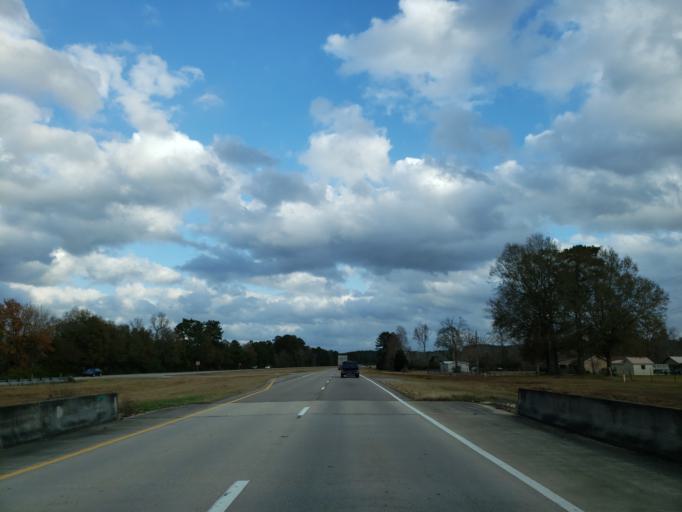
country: US
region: Mississippi
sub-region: Forrest County
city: Petal
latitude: 31.2310
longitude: -89.1955
